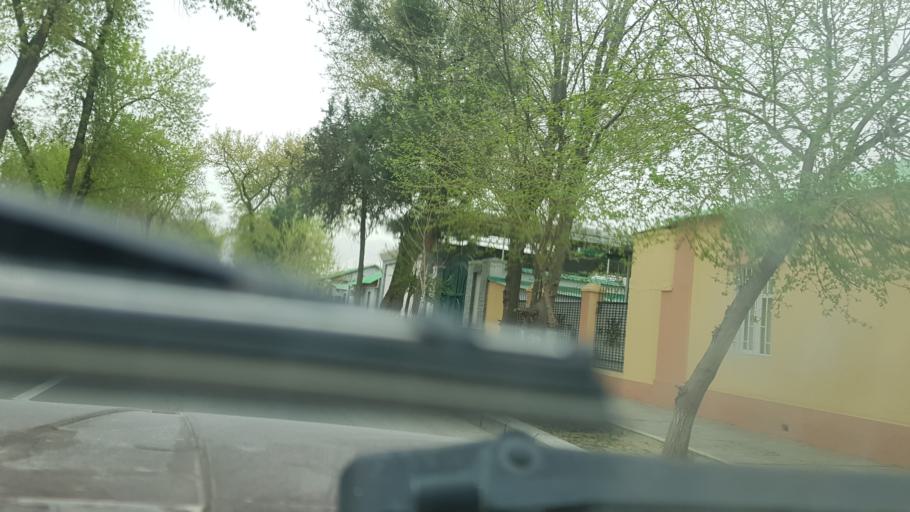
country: TM
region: Ahal
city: Ashgabat
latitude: 37.9525
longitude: 58.3637
